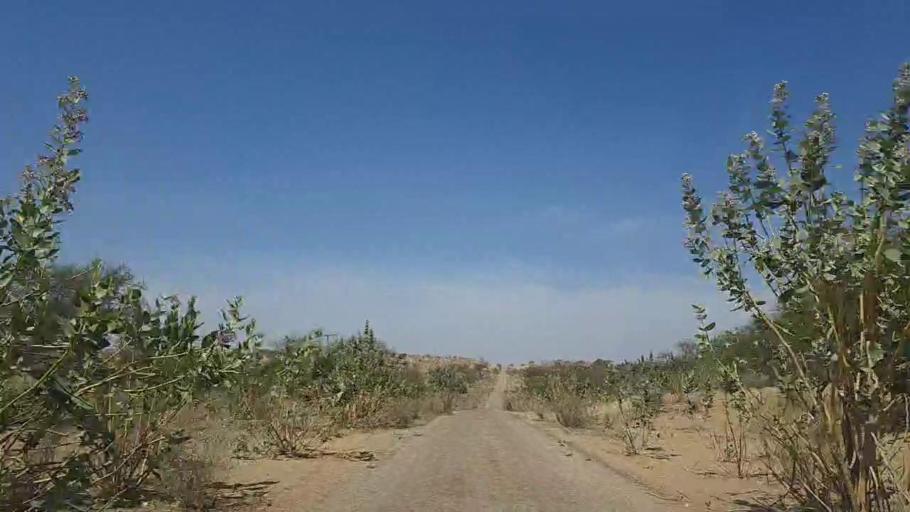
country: PK
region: Sindh
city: Mithi
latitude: 24.8548
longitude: 69.6702
